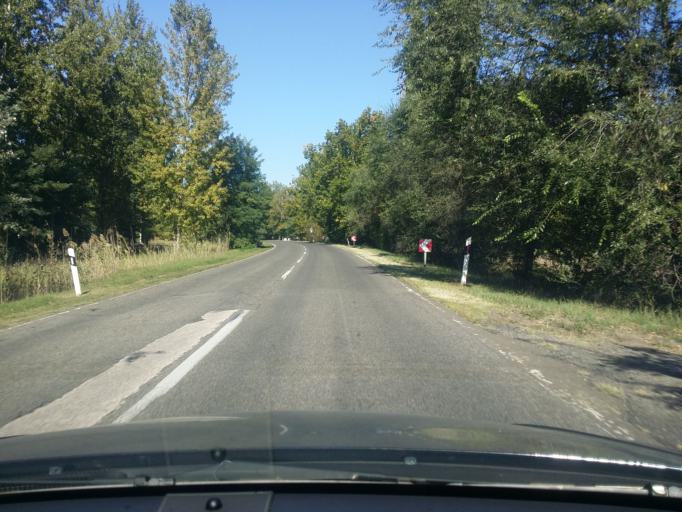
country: HU
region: Csongrad
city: Pusztaszer
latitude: 46.5222
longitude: 19.9679
